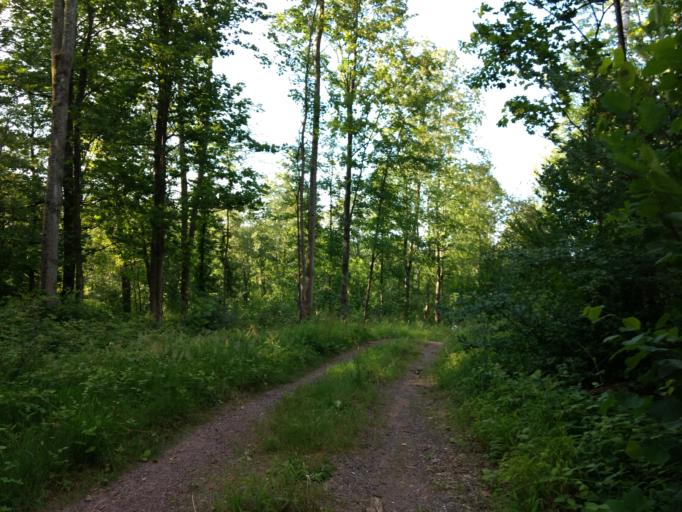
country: DE
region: Saarland
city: Beckingen
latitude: 49.3910
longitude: 6.6971
